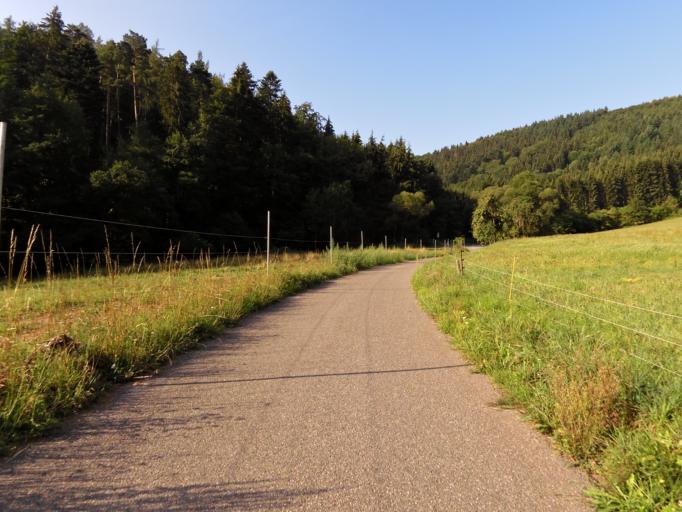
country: DE
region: Bavaria
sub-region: Regierungsbezirk Unterfranken
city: Kirchzell
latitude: 49.6006
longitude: 9.1963
